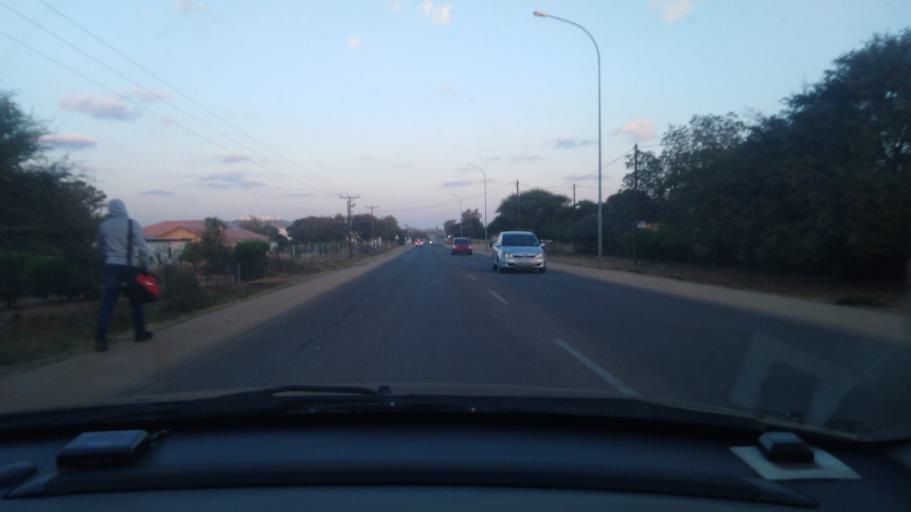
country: BW
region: Central
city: Mahalapye
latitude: -23.1026
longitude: 26.8297
